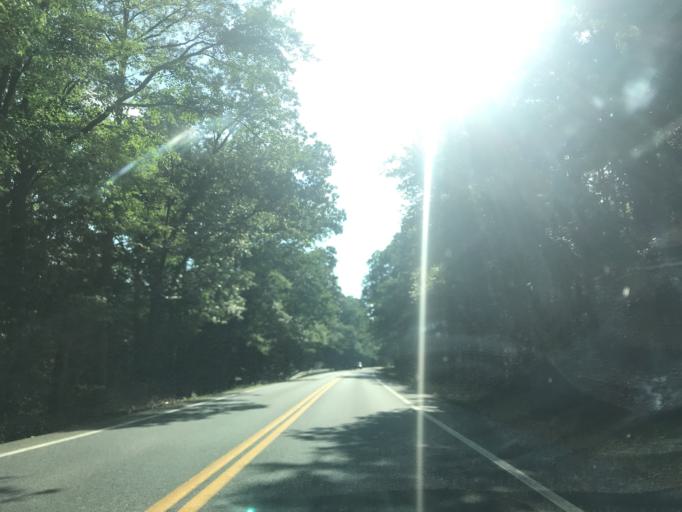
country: US
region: Maryland
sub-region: Wicomico County
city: Hebron
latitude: 38.4639
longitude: -75.7291
